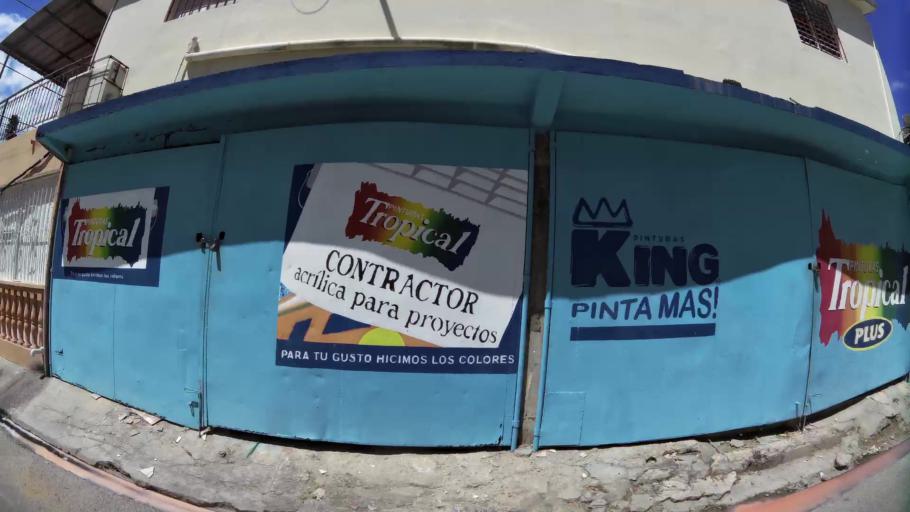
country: DO
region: San Cristobal
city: San Cristobal
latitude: 18.4160
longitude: -70.0958
